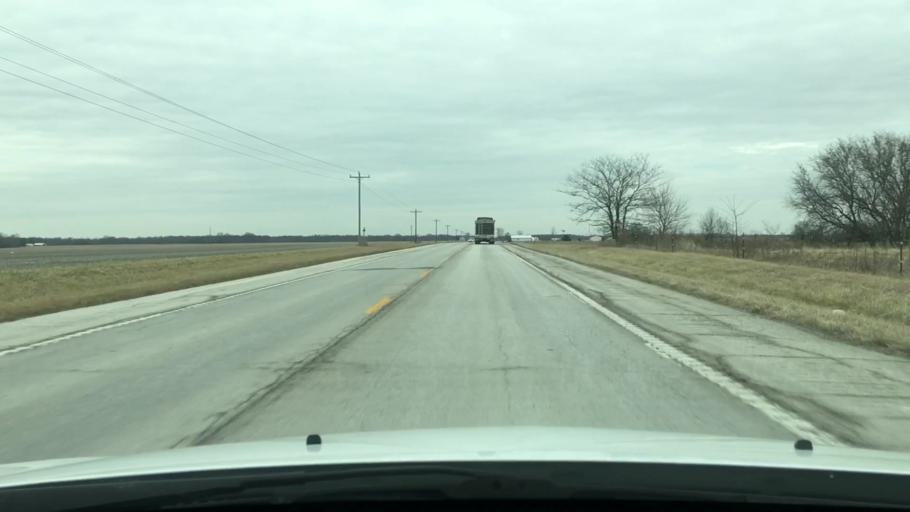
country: US
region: Missouri
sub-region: Montgomery County
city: Wellsville
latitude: 39.1806
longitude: -91.6473
